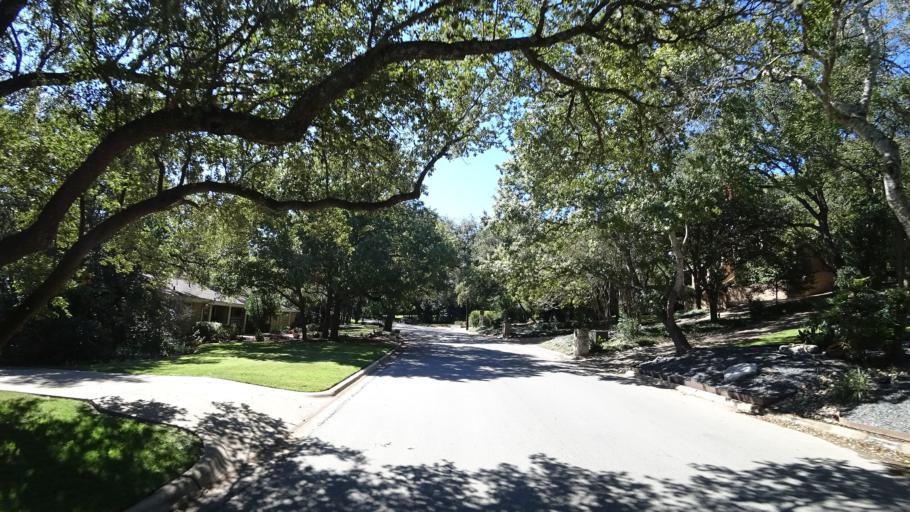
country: US
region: Texas
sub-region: Travis County
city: West Lake Hills
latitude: 30.3293
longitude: -97.7690
